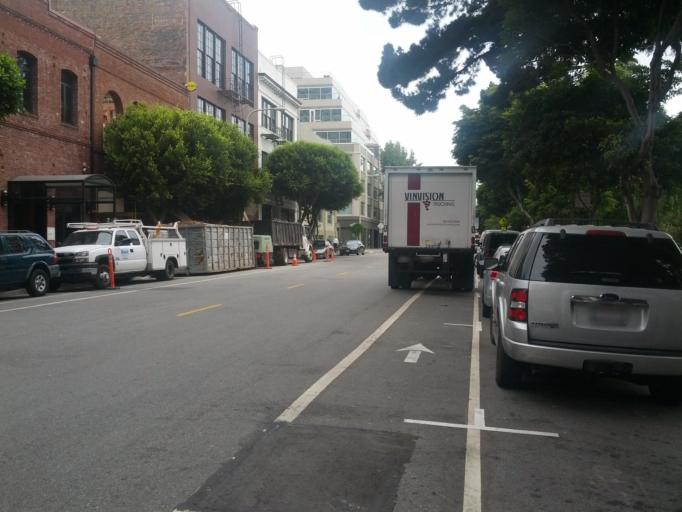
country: US
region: California
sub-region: San Francisco County
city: San Francisco
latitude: 37.7971
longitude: -122.3995
